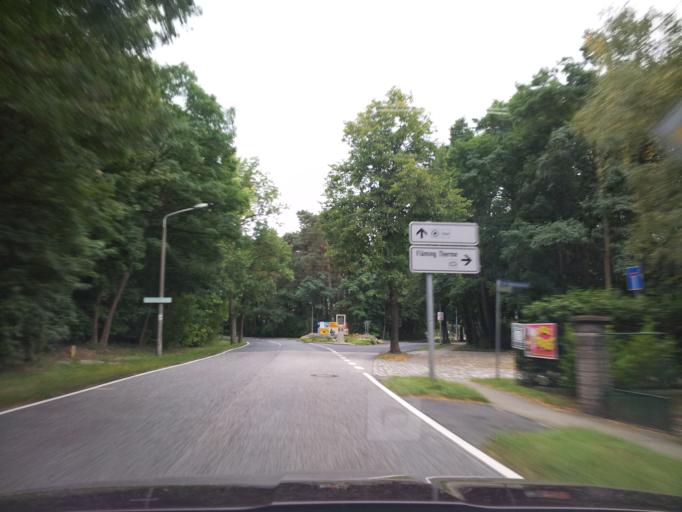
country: DE
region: Brandenburg
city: Luckenwalde
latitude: 52.1075
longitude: 13.1476
